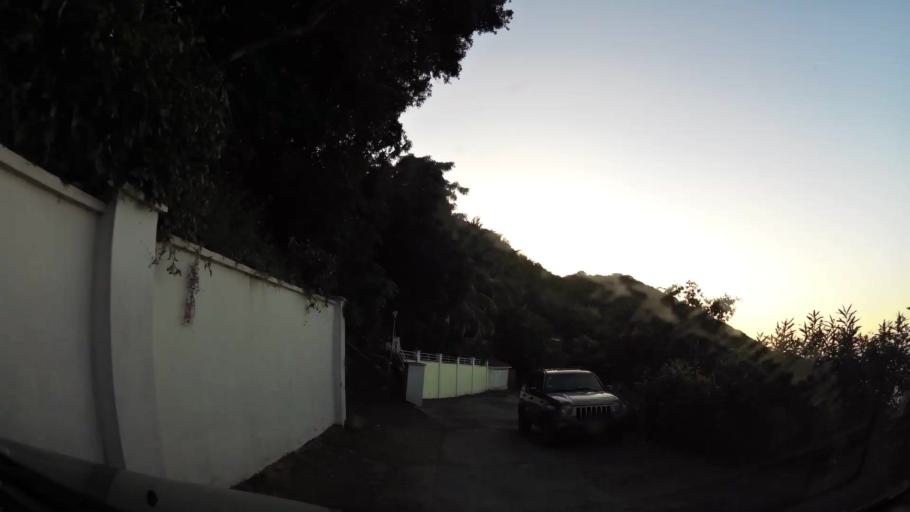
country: VG
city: Tortola
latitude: 18.4480
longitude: -64.5776
